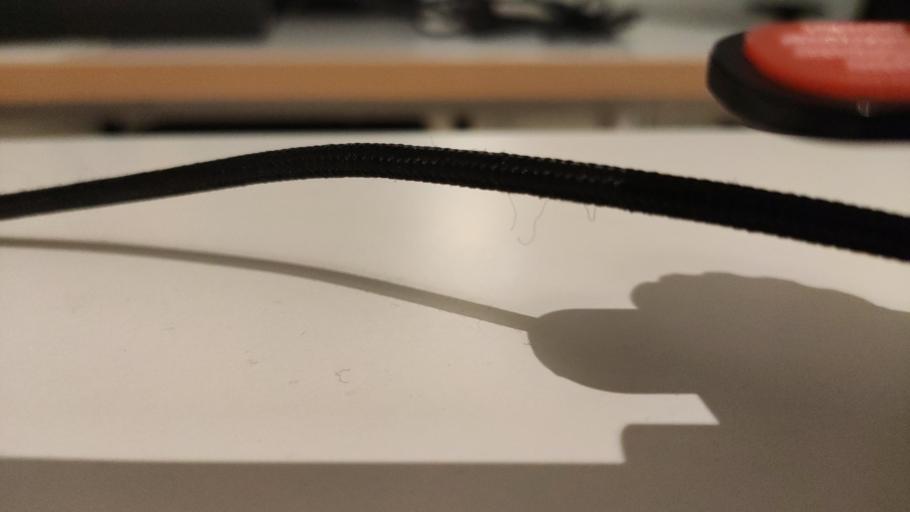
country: RU
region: Moskovskaya
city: Rogachevo
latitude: 56.4188
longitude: 37.2109
